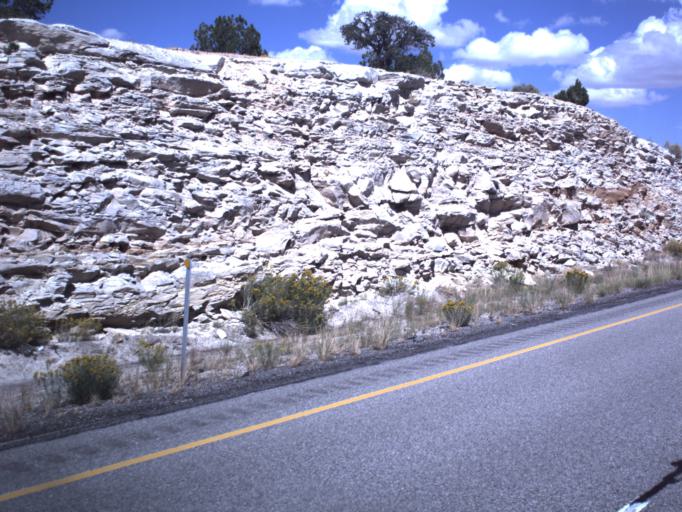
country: US
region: Utah
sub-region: Emery County
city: Ferron
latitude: 38.8474
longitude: -110.8884
